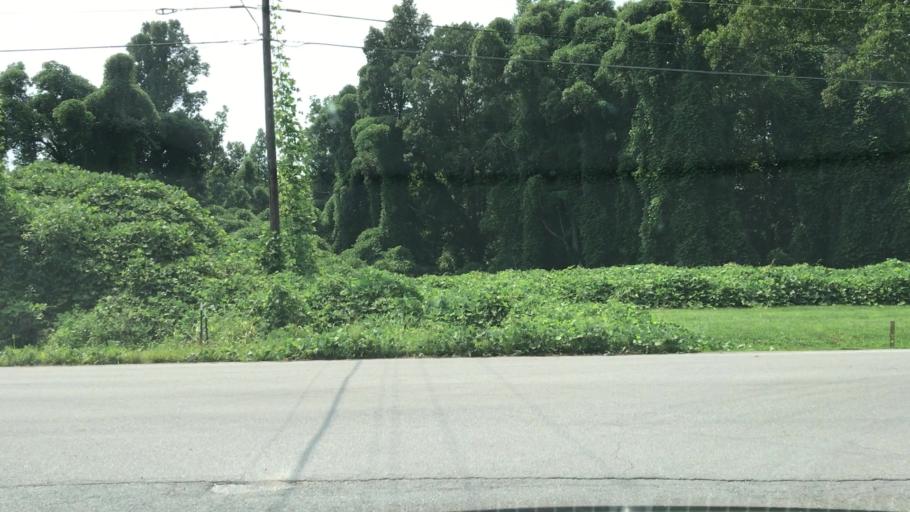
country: US
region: Tennessee
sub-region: Sumner County
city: Portland
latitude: 36.5215
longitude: -86.5014
